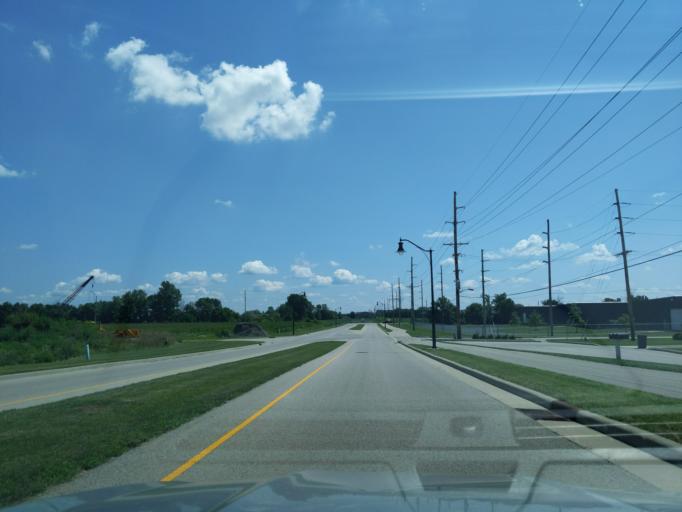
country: US
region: Indiana
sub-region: Decatur County
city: Greensburg
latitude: 39.3586
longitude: -85.4924
